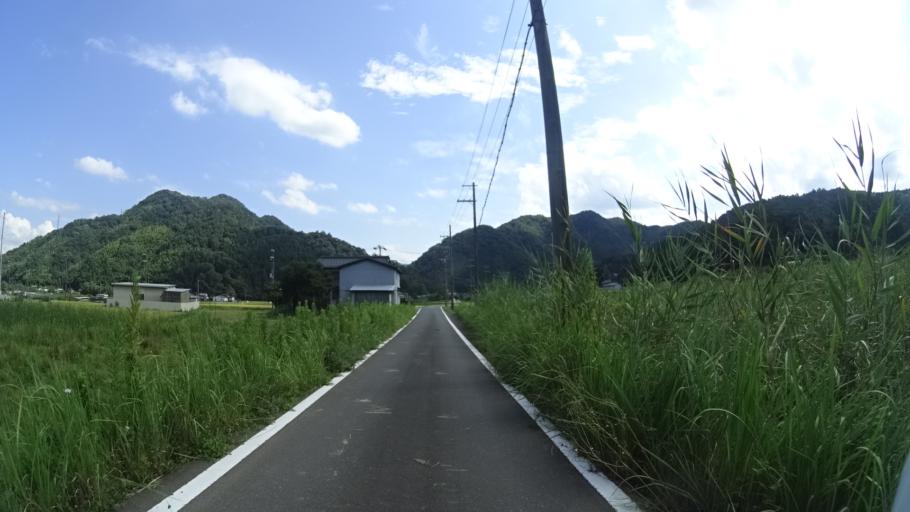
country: JP
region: Kyoto
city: Maizuru
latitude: 35.4335
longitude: 135.2963
